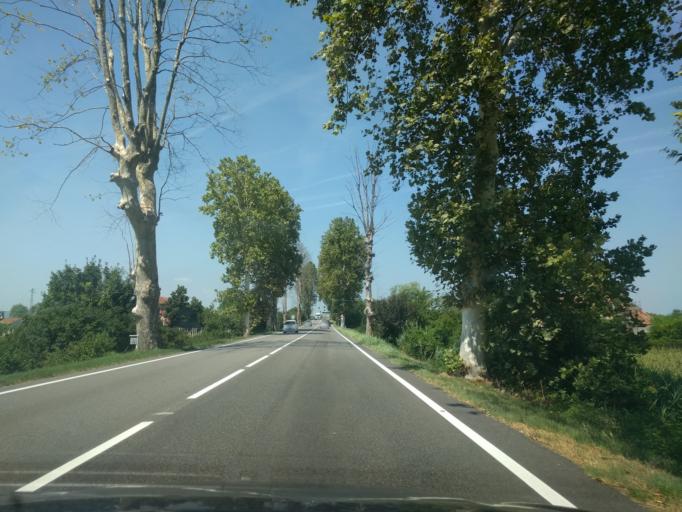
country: IT
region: Veneto
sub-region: Provincia di Padova
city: Stanghella
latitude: 45.1420
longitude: 11.7570
